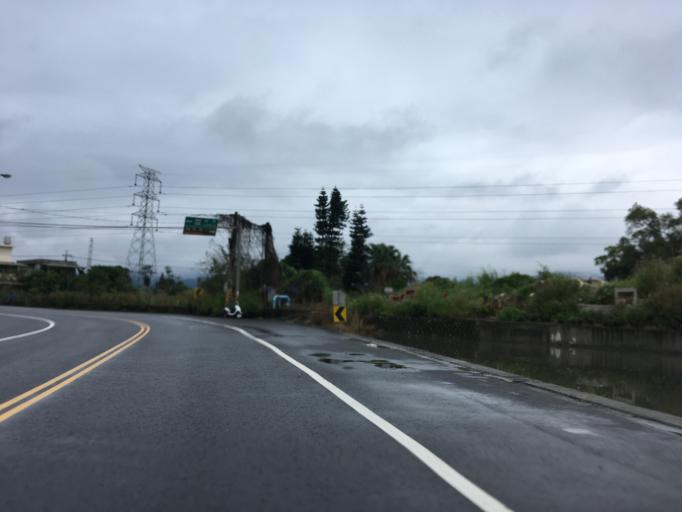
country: TW
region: Taiwan
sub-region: Yilan
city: Yilan
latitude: 24.6648
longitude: 121.7498
